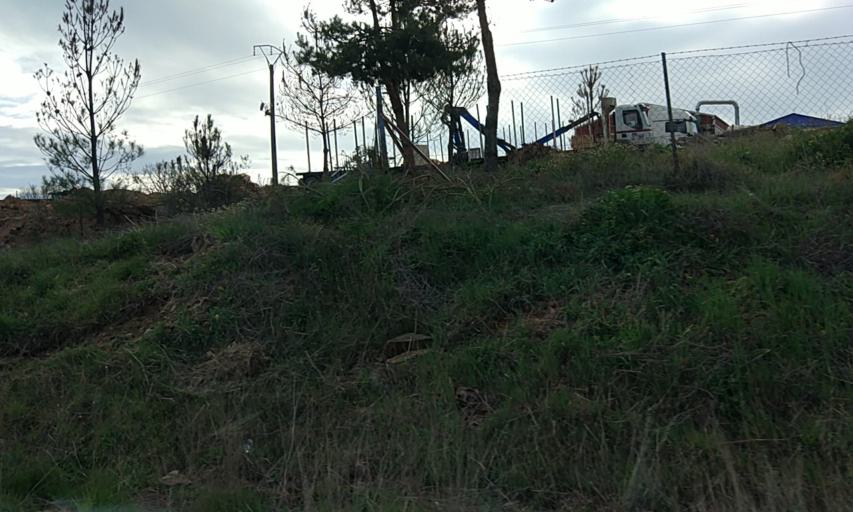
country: ES
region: Castille and Leon
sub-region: Provincia de Salamanca
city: Robleda
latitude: 40.3757
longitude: -6.6142
